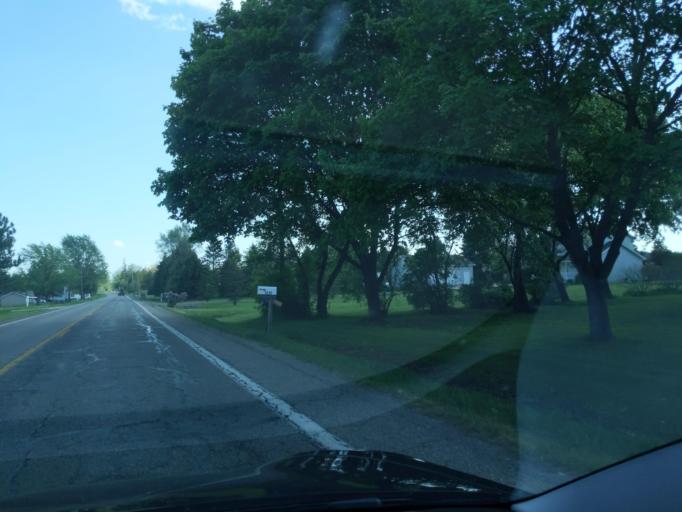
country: US
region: Michigan
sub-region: Eaton County
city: Potterville
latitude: 42.6865
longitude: -84.7396
